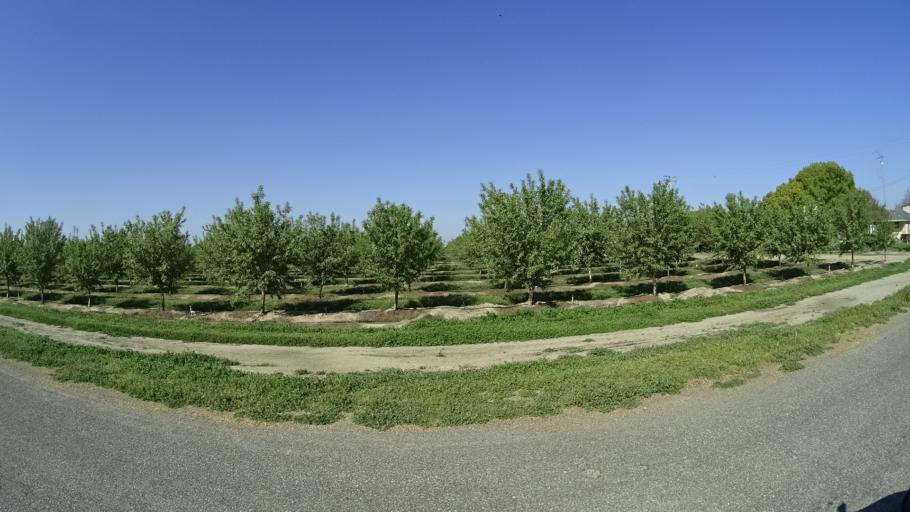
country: US
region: California
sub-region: Glenn County
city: Hamilton City
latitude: 39.6262
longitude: -122.0275
